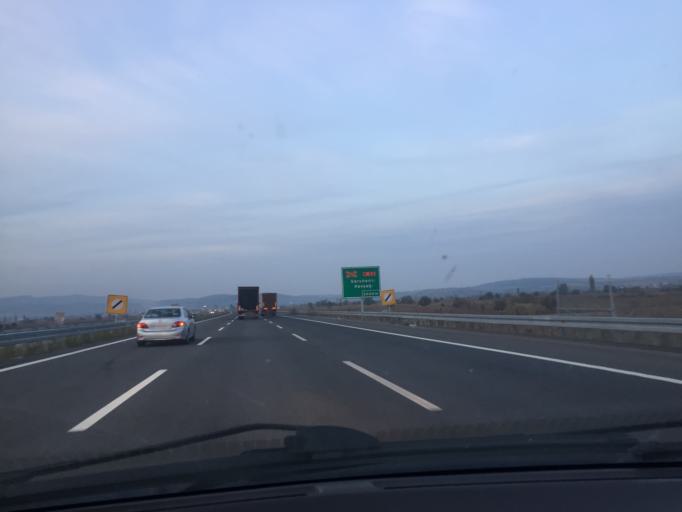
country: TR
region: Manisa
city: Halitpasa
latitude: 38.7456
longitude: 27.6592
